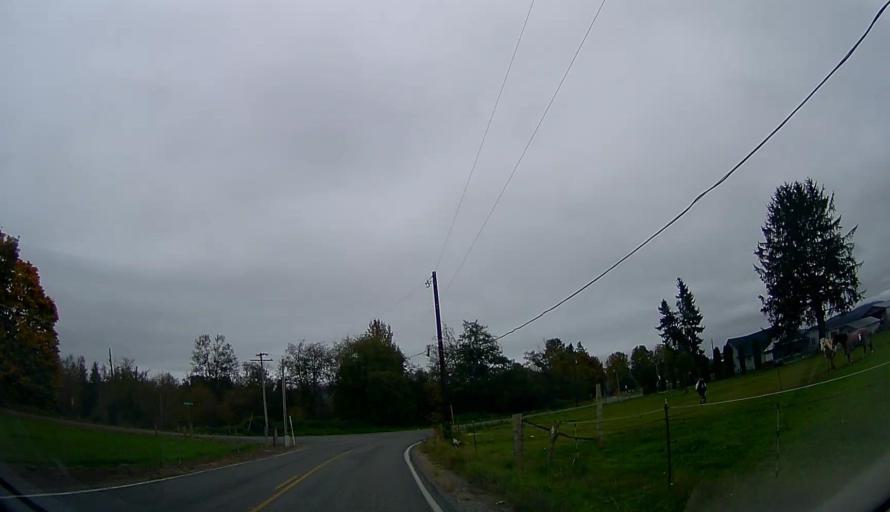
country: US
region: Washington
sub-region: Skagit County
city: Sedro-Woolley
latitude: 48.5158
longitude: -122.1399
